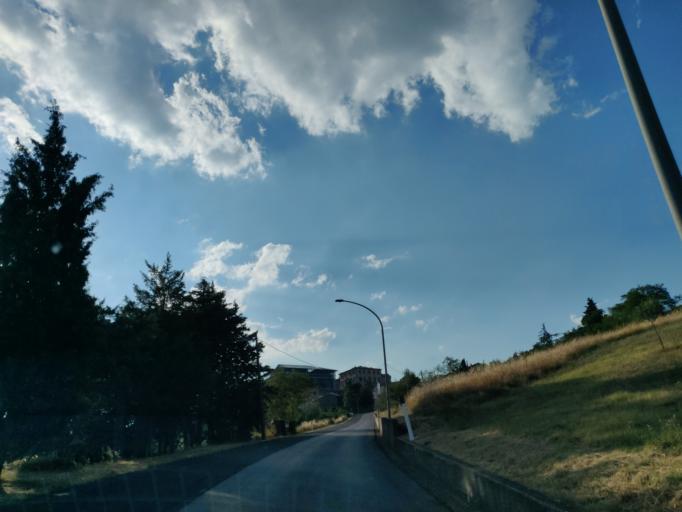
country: IT
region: Tuscany
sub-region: Provincia di Siena
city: Piancastagnaio
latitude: 42.8461
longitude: 11.6973
